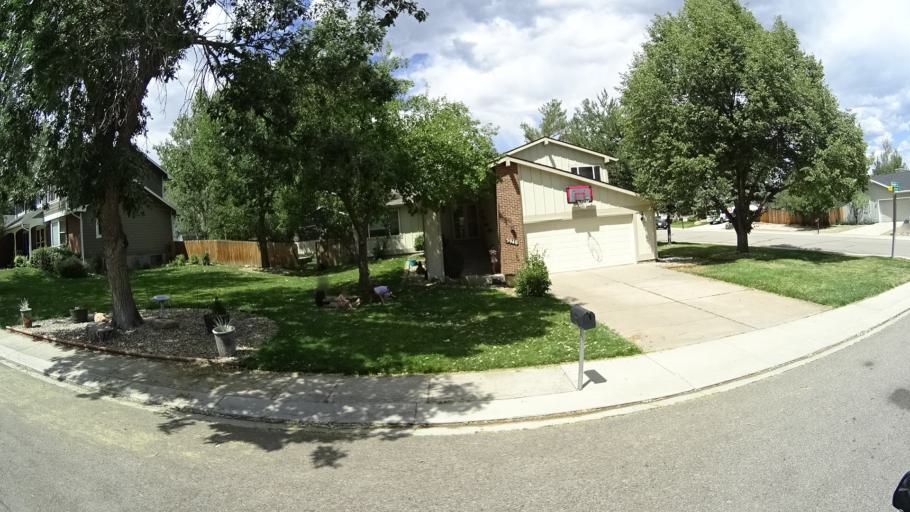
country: US
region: Colorado
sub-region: El Paso County
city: Stratmoor
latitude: 38.7725
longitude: -104.8189
